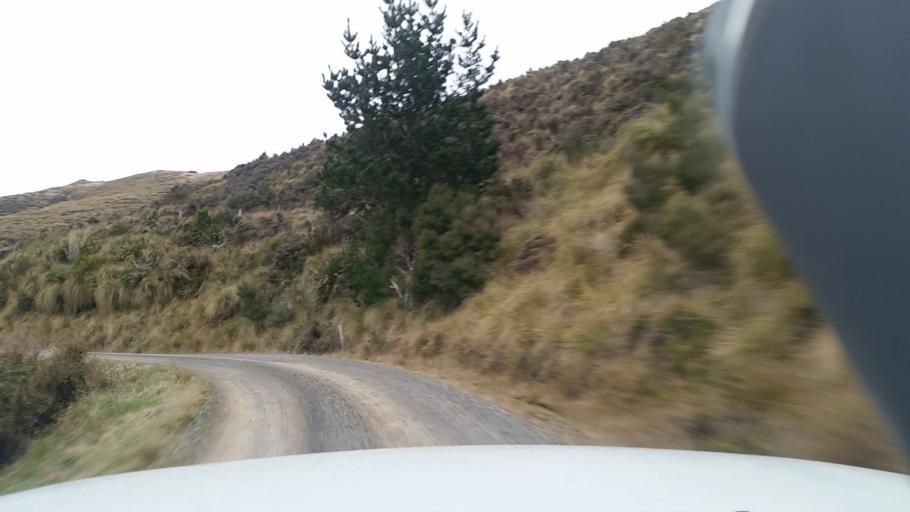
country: NZ
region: Canterbury
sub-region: Christchurch City
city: Christchurch
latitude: -43.8107
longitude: 172.8643
